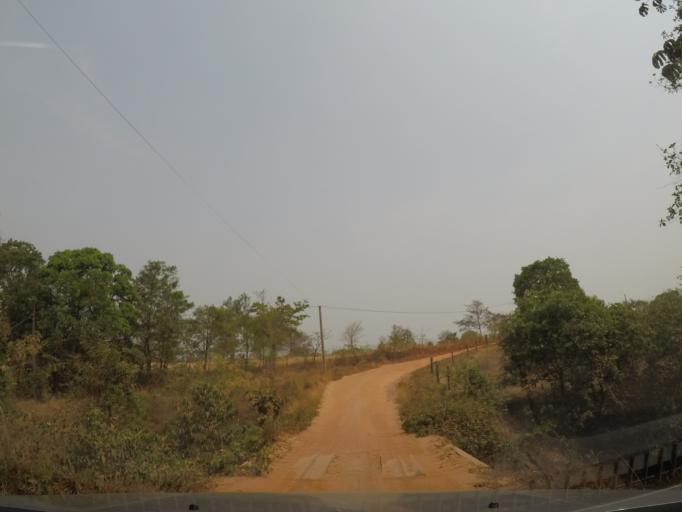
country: BR
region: Goias
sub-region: Pirenopolis
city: Pirenopolis
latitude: -15.8363
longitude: -48.9523
